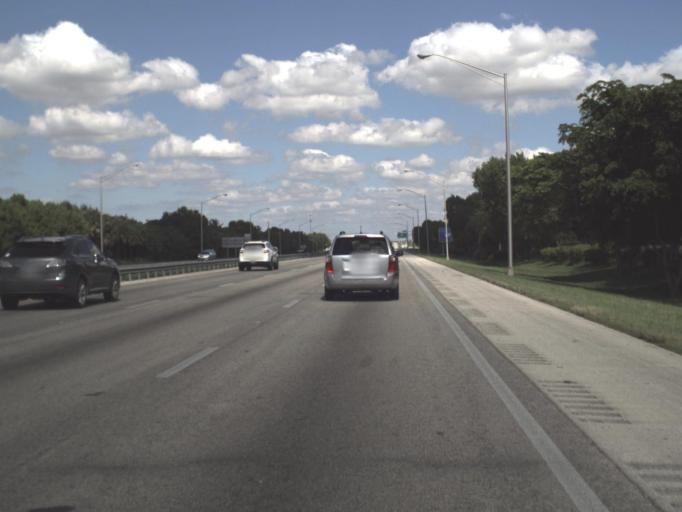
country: US
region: Florida
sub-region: Miami-Dade County
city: The Crossings
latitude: 25.6748
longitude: -80.3885
